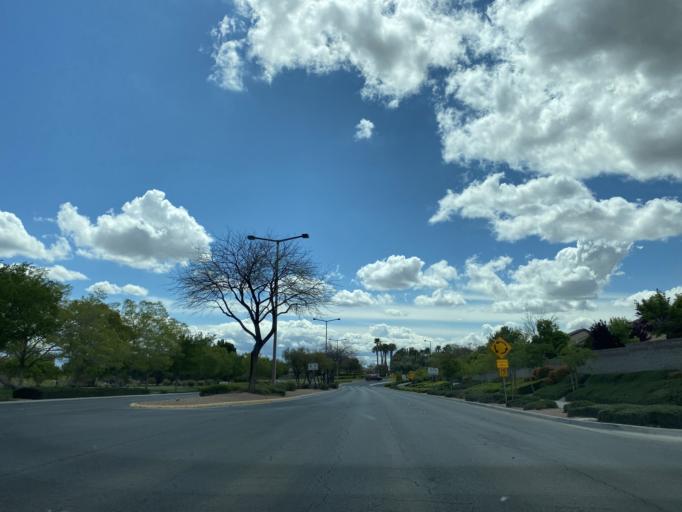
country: US
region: Nevada
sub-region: Clark County
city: Summerlin South
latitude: 36.1802
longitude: -115.3192
